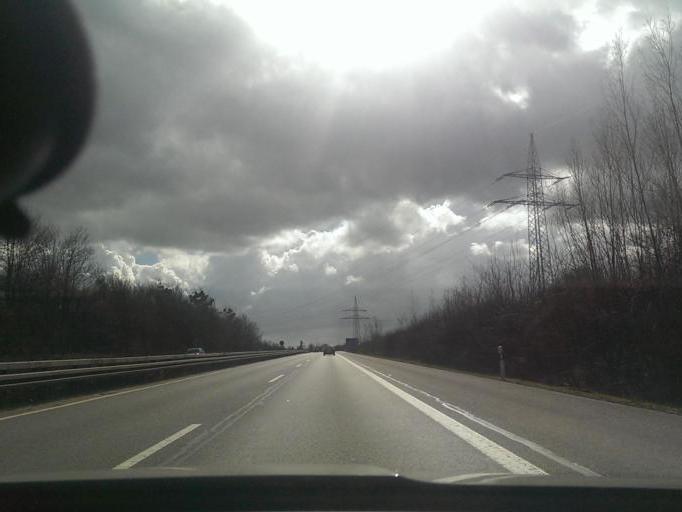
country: DE
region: Lower Saxony
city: Wolfsburg
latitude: 52.4088
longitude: 10.7337
